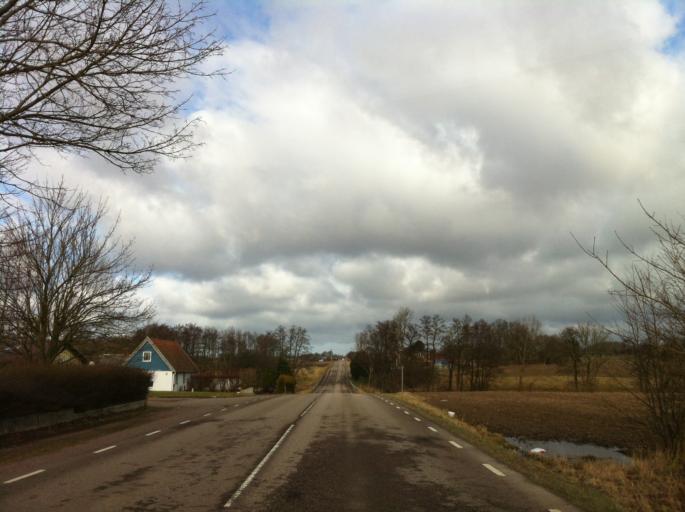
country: SE
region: Skane
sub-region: Helsingborg
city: Hyllinge
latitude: 56.1273
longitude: 12.8813
